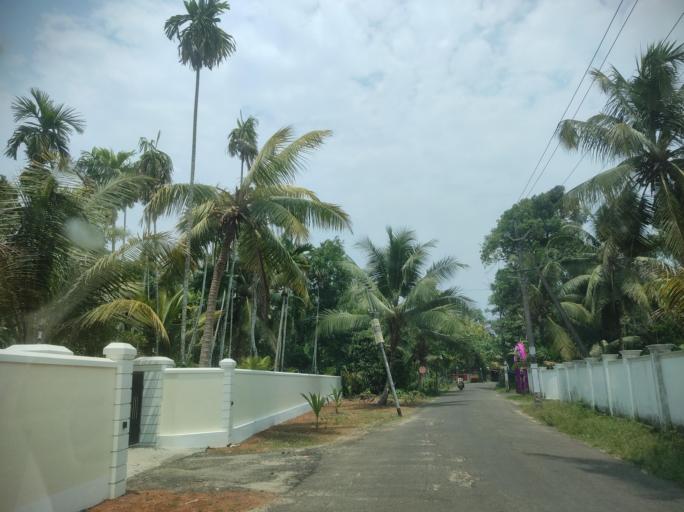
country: IN
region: Kerala
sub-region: Alappuzha
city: Vayalar
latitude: 9.7477
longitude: 76.3247
